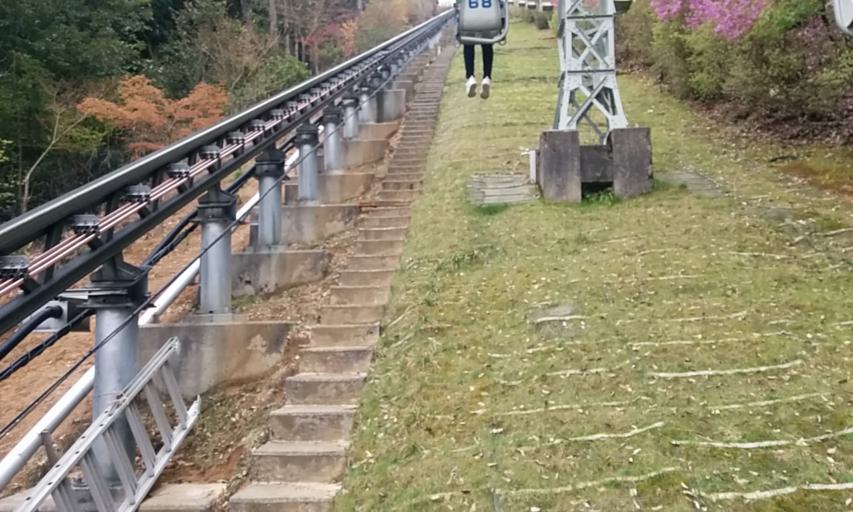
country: JP
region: Kyoto
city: Miyazu
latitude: 35.5538
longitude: 135.1827
